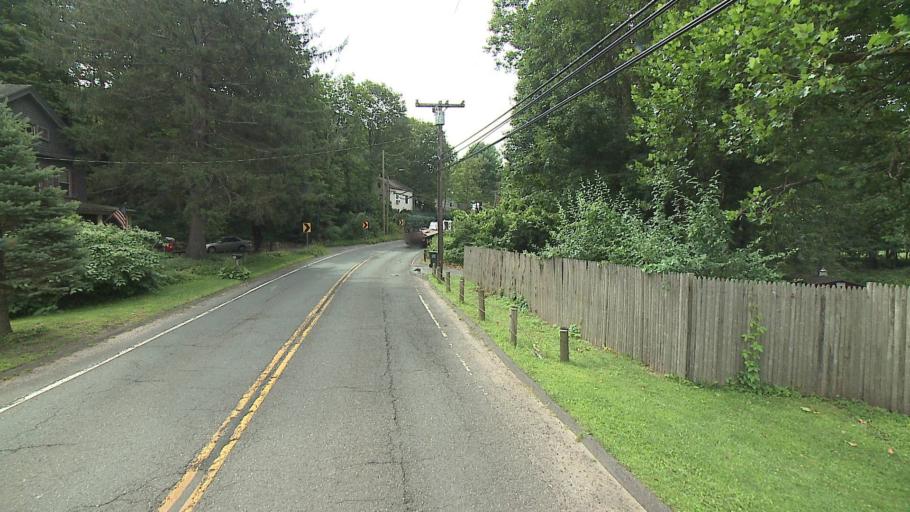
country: US
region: Connecticut
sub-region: Litchfield County
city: Woodbury
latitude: 41.5647
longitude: -73.2153
